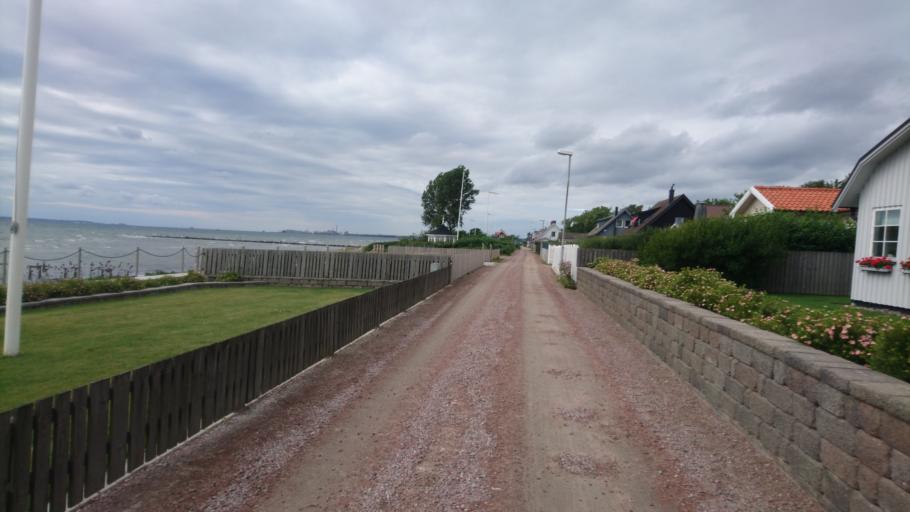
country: SE
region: Skane
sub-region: Helsingborg
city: Rydeback
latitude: 55.9565
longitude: 12.7587
